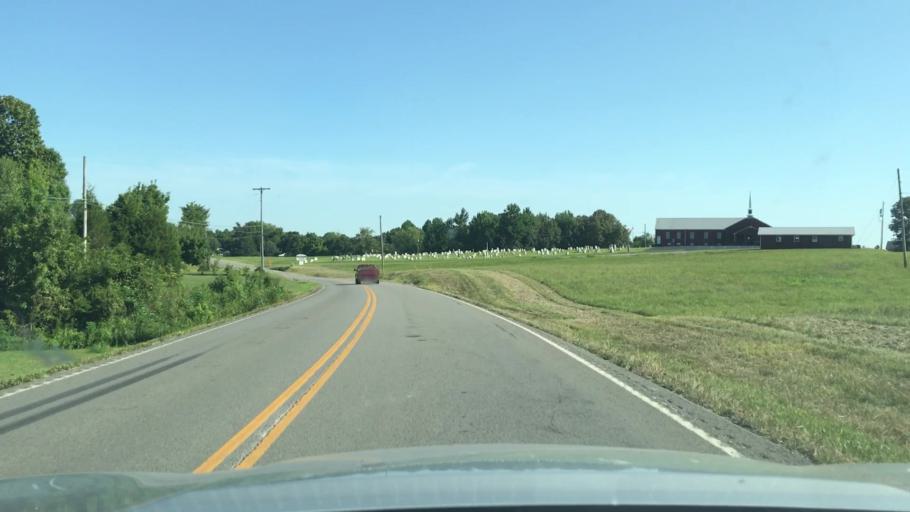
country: US
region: Kentucky
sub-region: Muhlenberg County
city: Greenville
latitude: 37.1783
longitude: -87.1525
